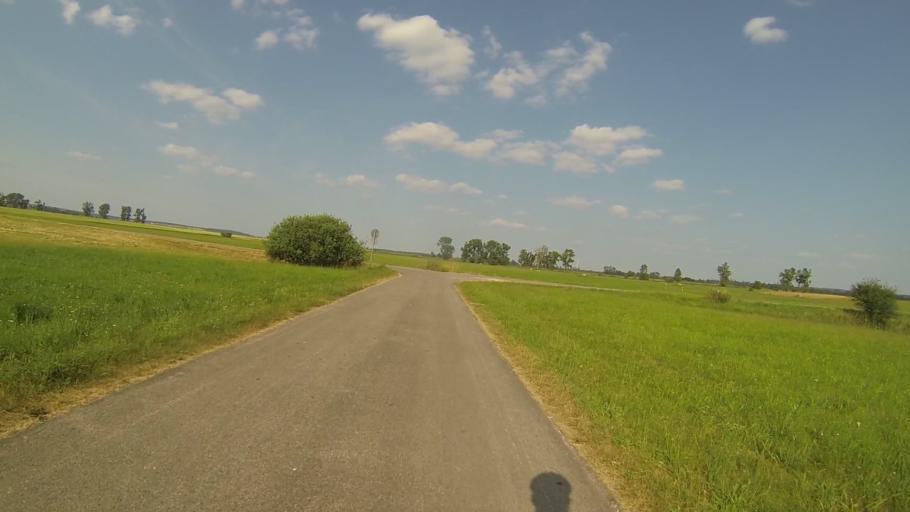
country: DE
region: Baden-Wuerttemberg
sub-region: Tuebingen Region
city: Asselfingen
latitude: 48.4997
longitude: 10.2152
